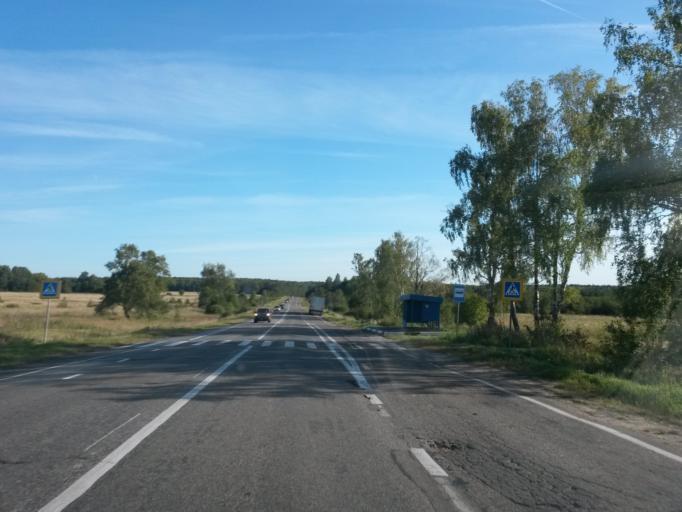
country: RU
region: Jaroslavl
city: Gavrilov-Yam
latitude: 57.4461
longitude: 39.9150
